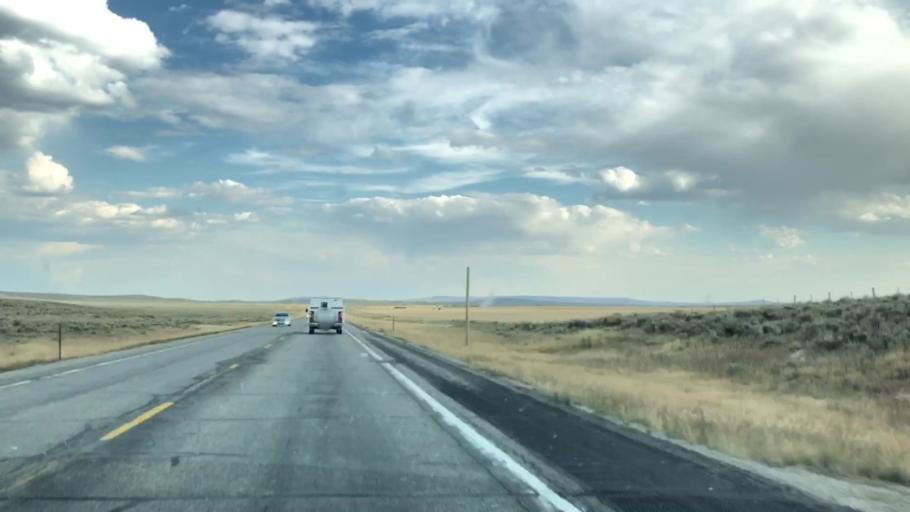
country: US
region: Wyoming
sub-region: Sublette County
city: Pinedale
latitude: 43.0452
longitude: -110.1457
